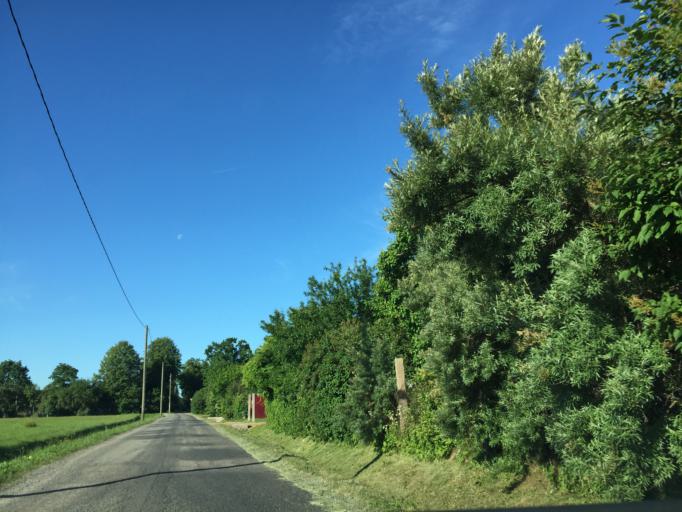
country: LV
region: Ventspils
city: Ventspils
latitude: 57.3673
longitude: 21.6070
